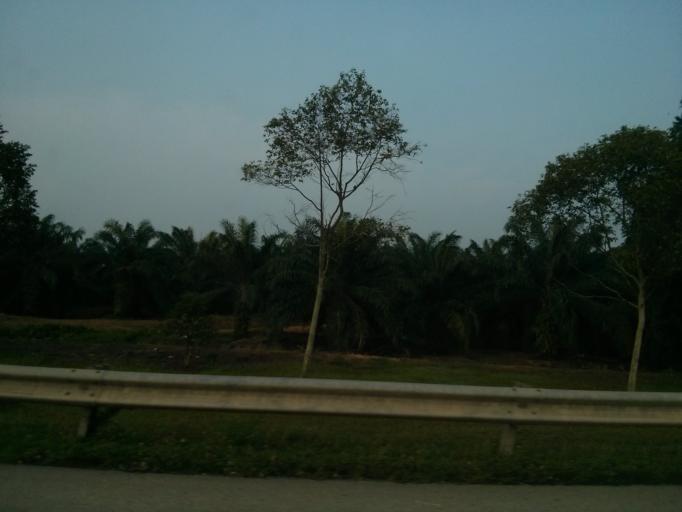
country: MY
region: Negeri Sembilan
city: Kampung Baharu Nilai
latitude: 2.7782
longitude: 101.6756
